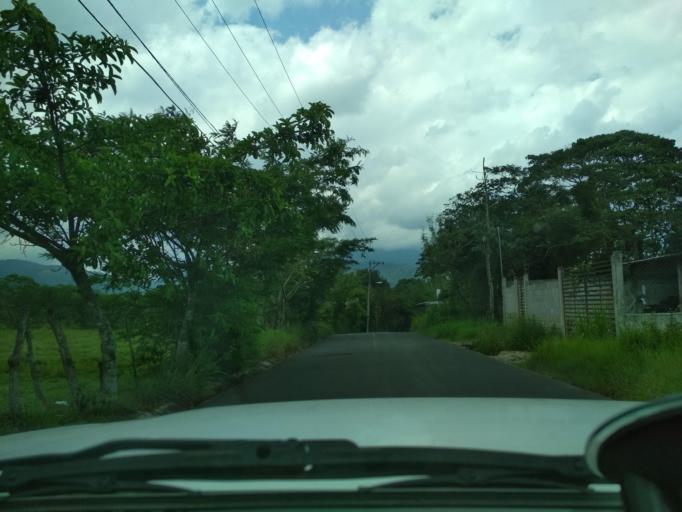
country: MX
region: Veracruz
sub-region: Cordoba
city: San Jose de Abajo [Unidad Habitacional]
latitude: 18.9229
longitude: -96.9597
